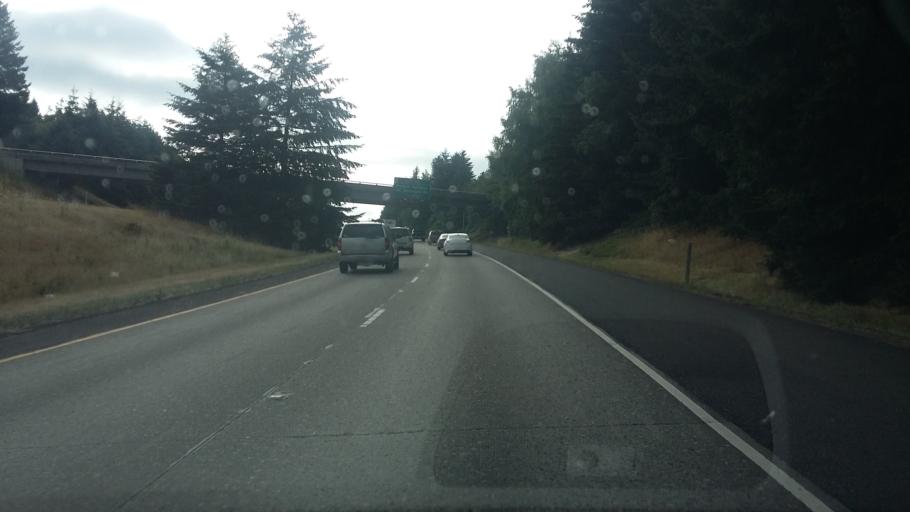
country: US
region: Washington
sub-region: Clark County
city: Barberton
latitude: 45.6995
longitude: -122.6224
